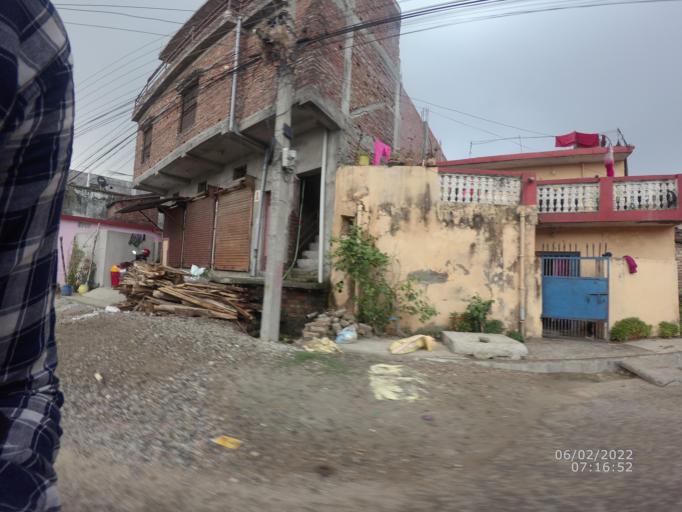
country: NP
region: Western Region
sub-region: Lumbini Zone
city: Bhairahawa
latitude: 27.4855
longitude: 83.4382
